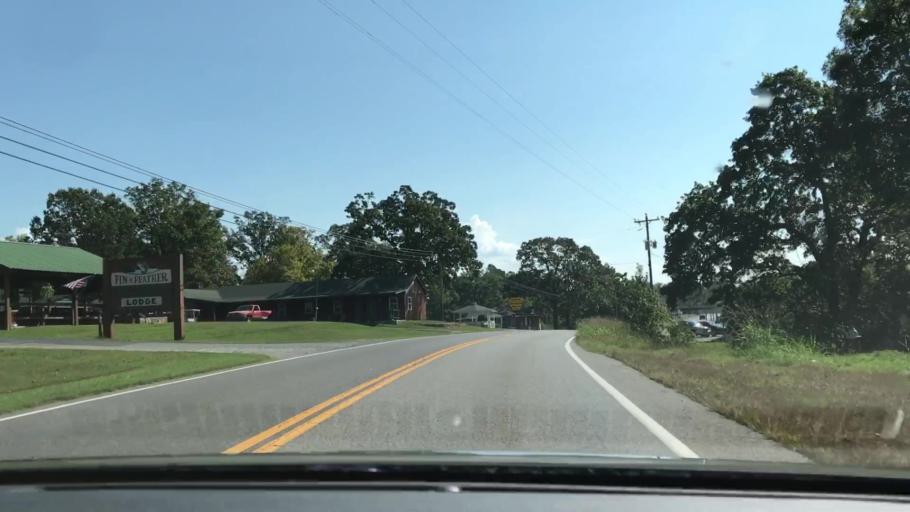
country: US
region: Kentucky
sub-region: Marshall County
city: Benton
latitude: 36.7768
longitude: -88.1450
